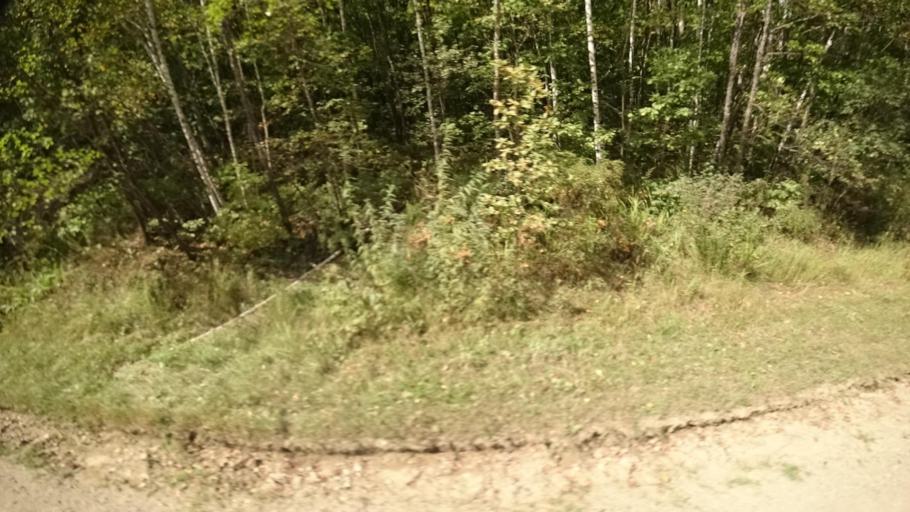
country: RU
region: Primorskiy
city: Yakovlevka
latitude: 44.6659
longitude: 133.6099
